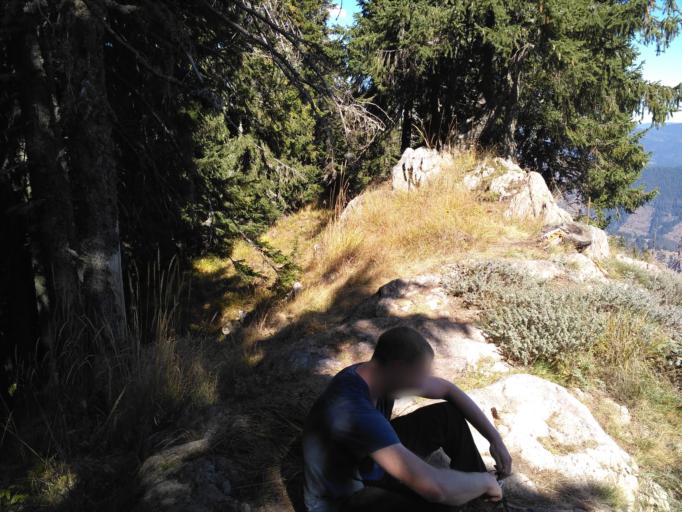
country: BG
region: Smolyan
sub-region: Obshtina Smolyan
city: Smolyan
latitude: 41.6381
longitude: 24.5496
